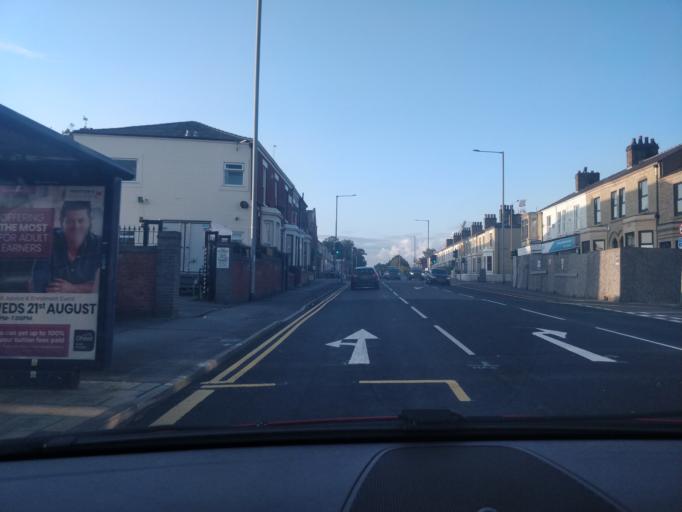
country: GB
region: England
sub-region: Lancashire
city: Preston
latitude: 53.7687
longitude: -2.6913
